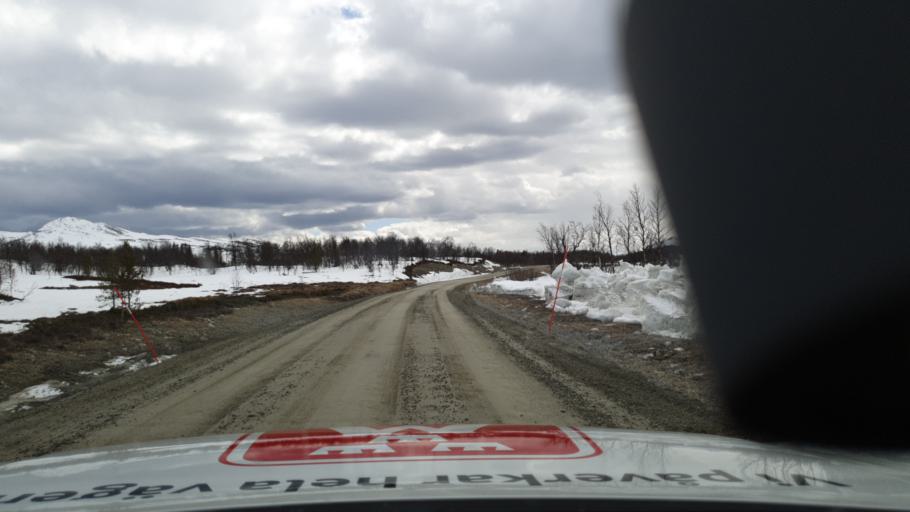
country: SE
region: Jaemtland
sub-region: Are Kommun
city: Are
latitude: 62.6265
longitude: 12.6329
